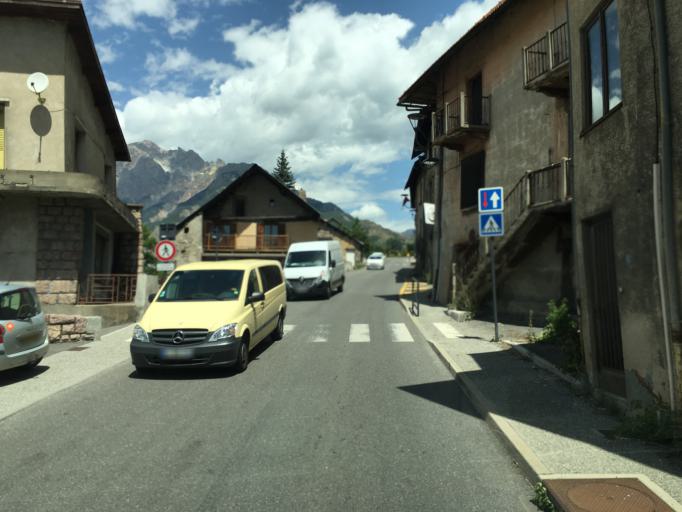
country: FR
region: Provence-Alpes-Cote d'Azur
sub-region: Departement des Hautes-Alpes
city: Saint-Martin-de-Queyrieres
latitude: 44.7948
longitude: 6.5626
